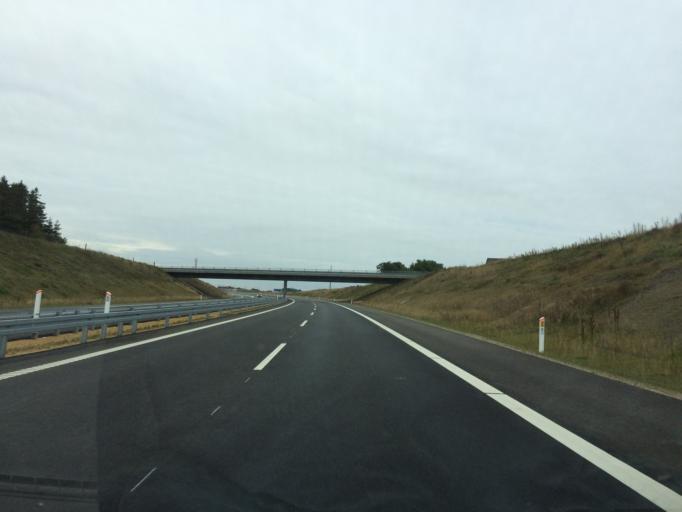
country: DK
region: Central Jutland
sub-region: Herning Kommune
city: Snejbjerg
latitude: 56.1356
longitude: 8.8699
